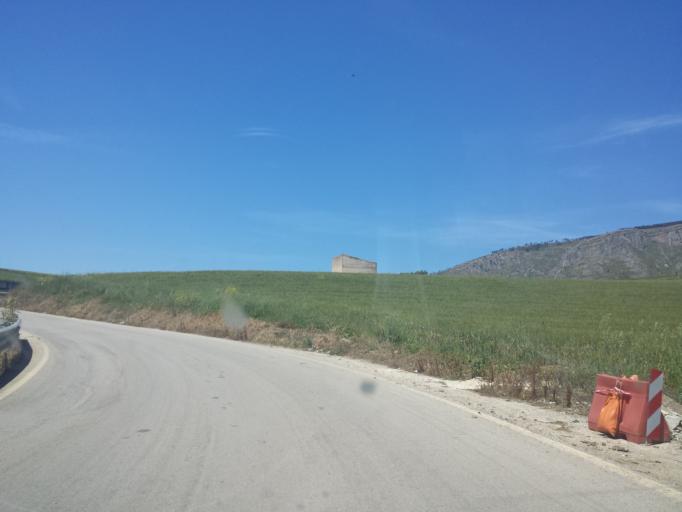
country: IT
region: Sicily
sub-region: Trapani
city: Alcamo
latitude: 37.9703
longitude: 12.9075
